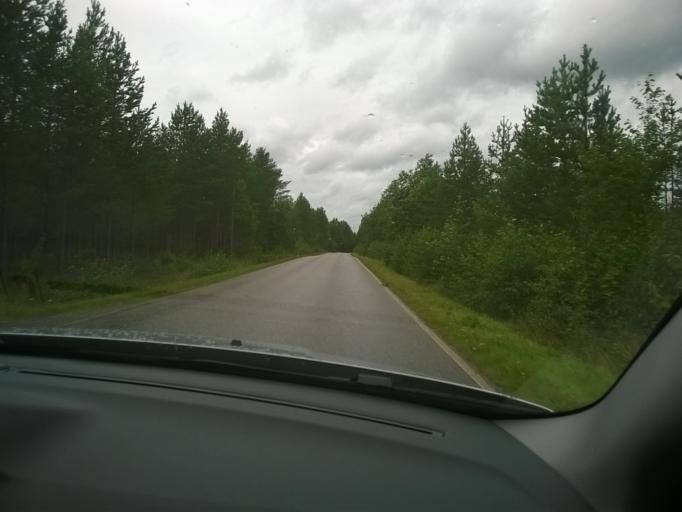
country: FI
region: Kainuu
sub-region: Kehys-Kainuu
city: Kuhmo
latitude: 64.1285
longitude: 29.4561
